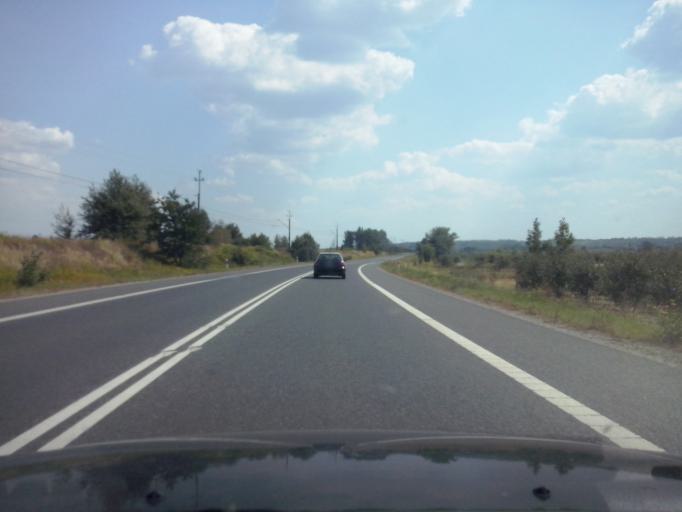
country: PL
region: Subcarpathian Voivodeship
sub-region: Powiat tarnobrzeski
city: Baranow Sandomierski
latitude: 50.5261
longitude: 21.5915
